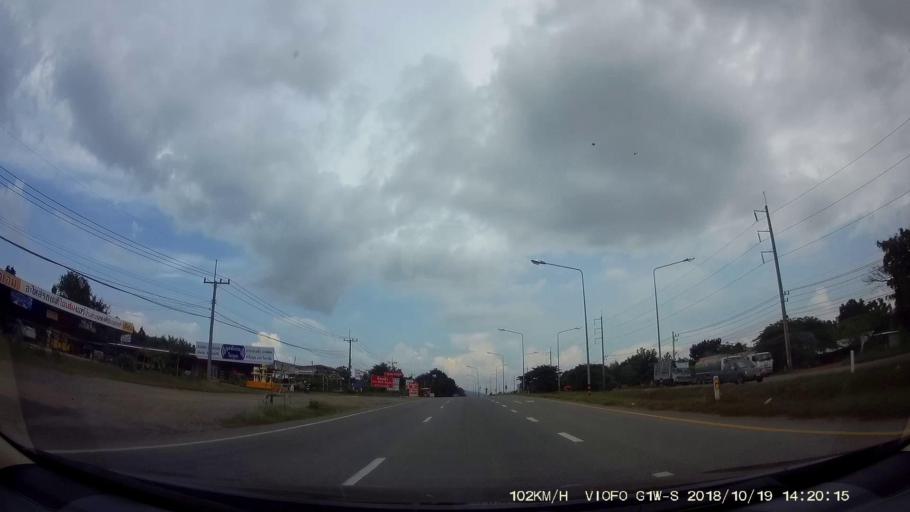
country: TH
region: Chaiyaphum
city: Kaeng Khro
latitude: 16.0380
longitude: 102.2539
